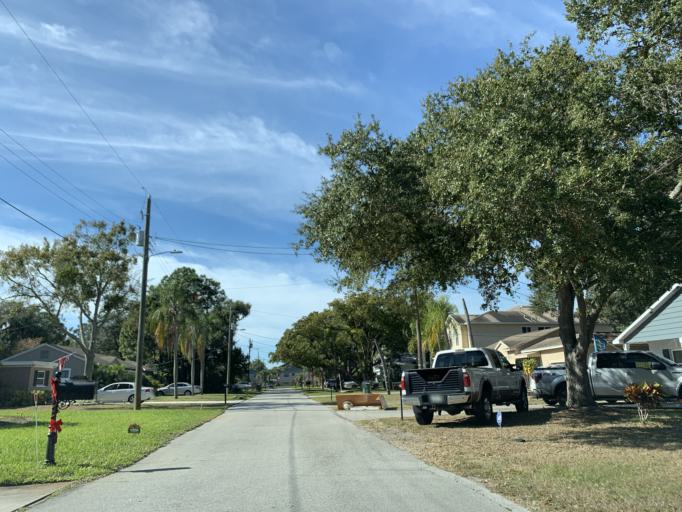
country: US
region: Florida
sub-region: Hillsborough County
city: Tampa
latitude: 27.8918
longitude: -82.4981
